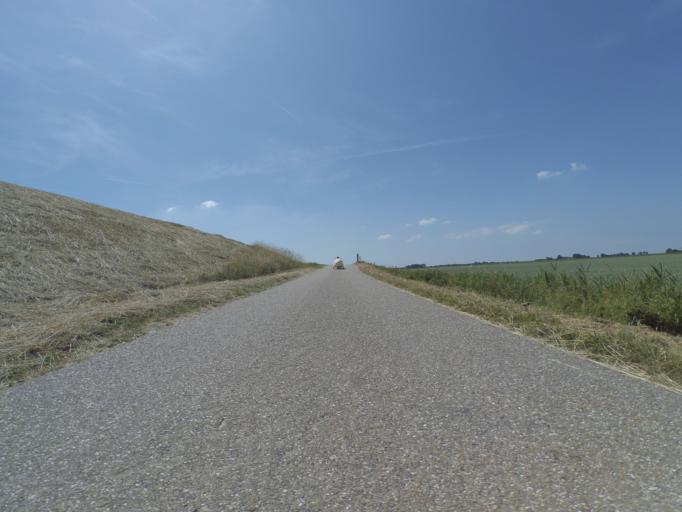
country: NL
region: North Brabant
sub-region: Gemeente Steenbergen
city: Nieuw-Vossemeer
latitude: 51.6369
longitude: 4.1803
